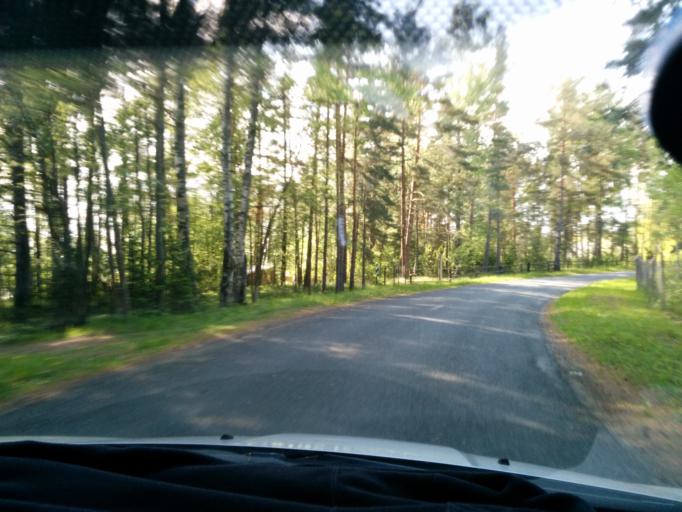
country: EE
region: Harju
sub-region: Loksa linn
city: Loksa
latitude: 59.6057
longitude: 25.7088
